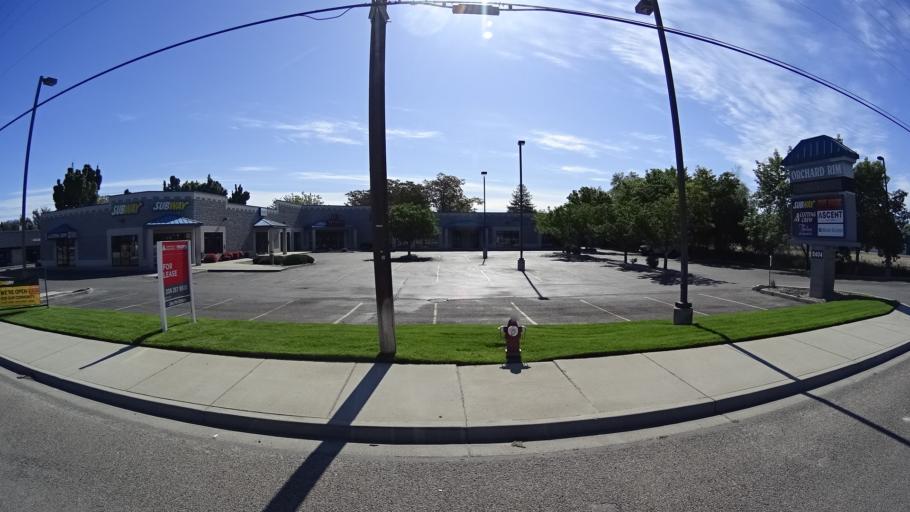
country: US
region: Idaho
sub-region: Ada County
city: Garden City
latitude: 43.5807
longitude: -116.2436
